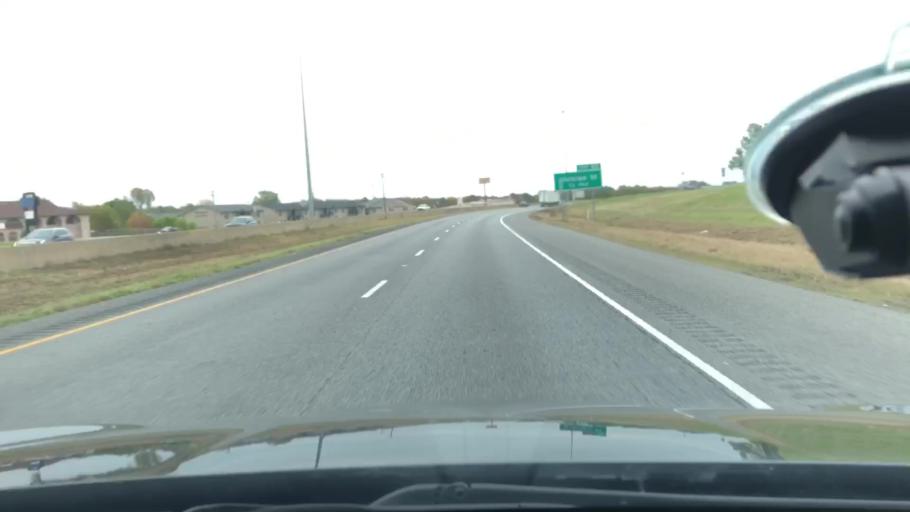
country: US
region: Texas
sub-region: Hunt County
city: Greenville
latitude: 33.1194
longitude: -96.0968
